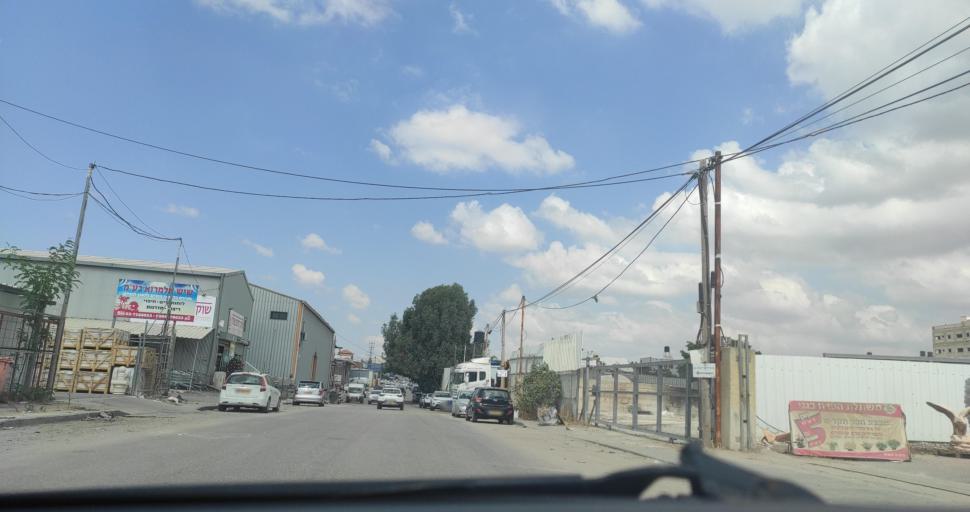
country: IL
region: Central District
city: Rosh Ha'Ayin
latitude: 32.1140
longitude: 34.9560
